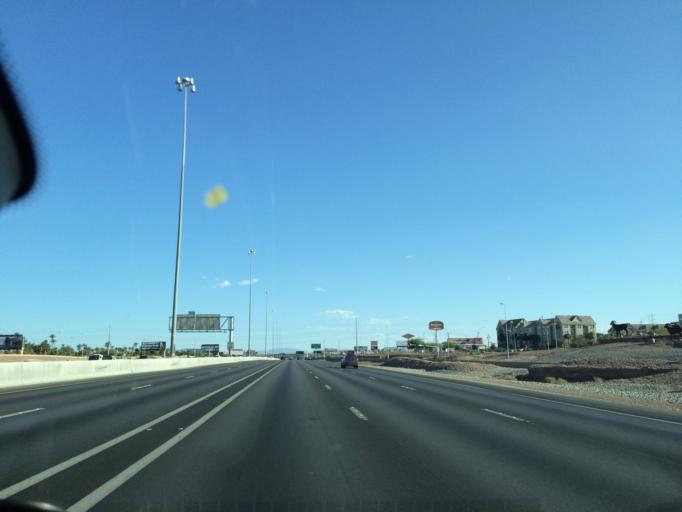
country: US
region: Nevada
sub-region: Clark County
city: Paradise
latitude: 36.0858
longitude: -115.1808
